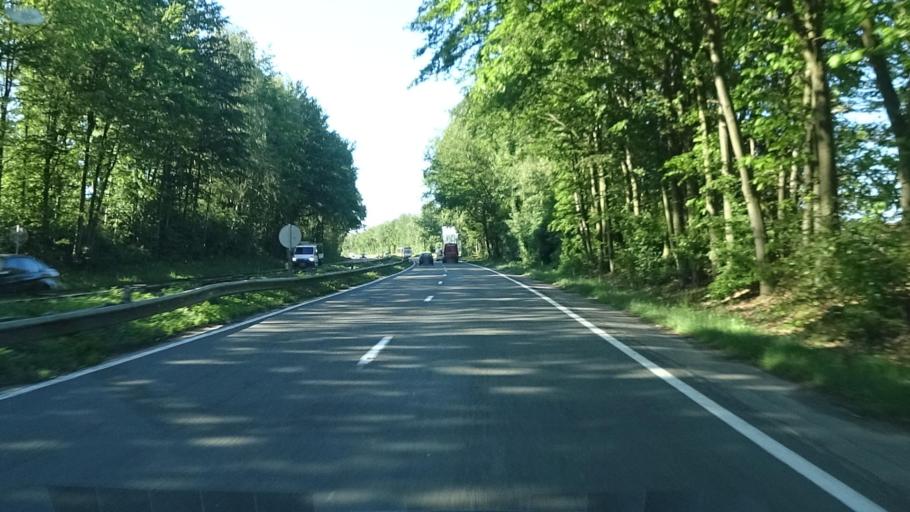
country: BE
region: Wallonia
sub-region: Province du Hainaut
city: Roeulx
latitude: 50.4694
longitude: 4.1386
